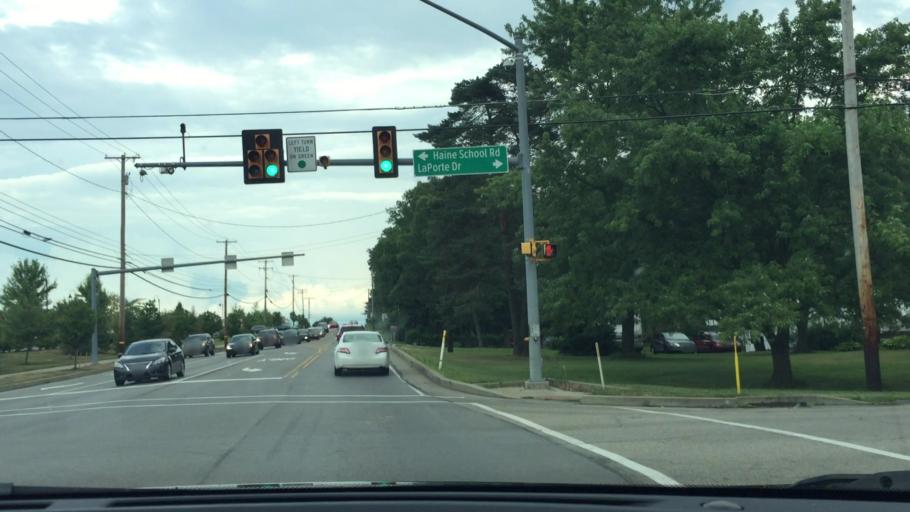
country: US
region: Pennsylvania
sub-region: Butler County
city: Fernway
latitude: 40.6820
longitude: -80.1252
